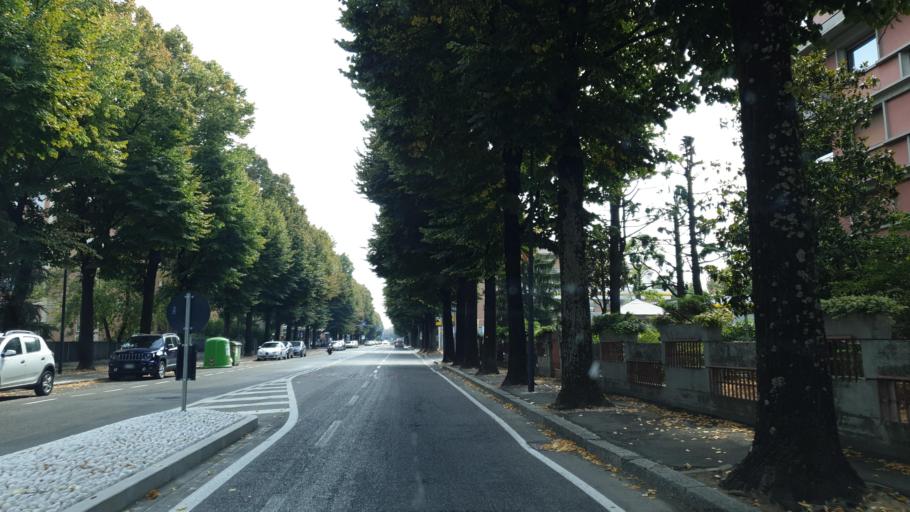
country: IT
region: Emilia-Romagna
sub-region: Provincia di Parma
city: Parma
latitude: 44.8035
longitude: 10.3045
